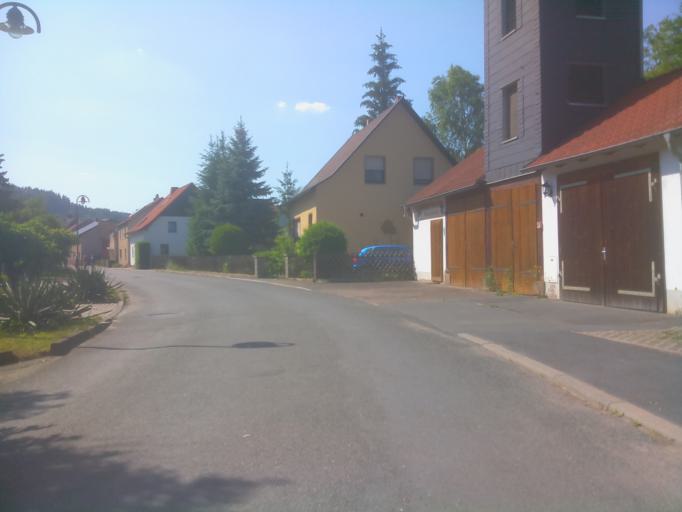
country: DE
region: Thuringia
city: Langenorla
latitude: 50.7411
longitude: 11.5776
